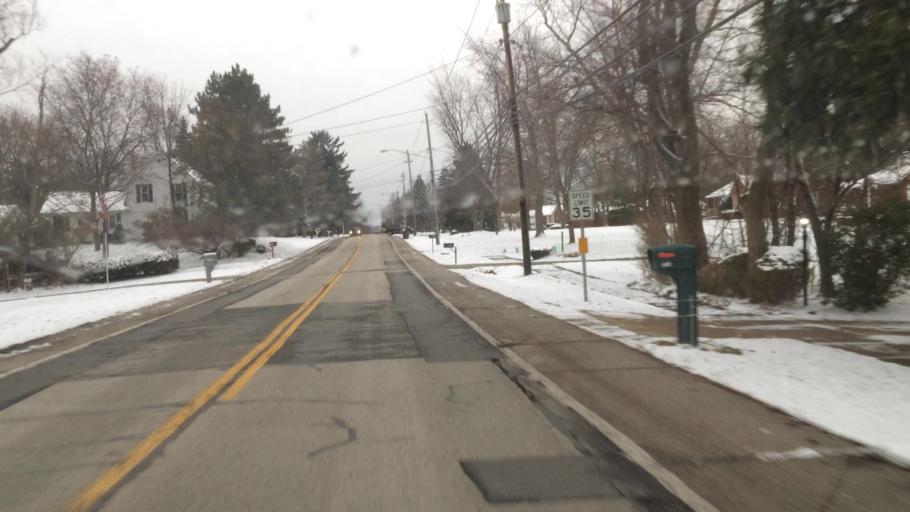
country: US
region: Ohio
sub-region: Cuyahoga County
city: Middleburg Heights
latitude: 41.3417
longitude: -81.8007
